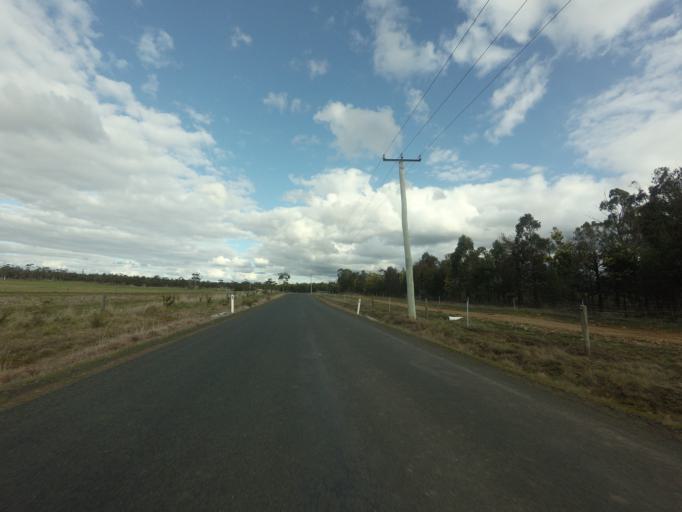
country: AU
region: Tasmania
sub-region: Northern Midlands
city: Longford
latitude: -41.8329
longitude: 147.2072
